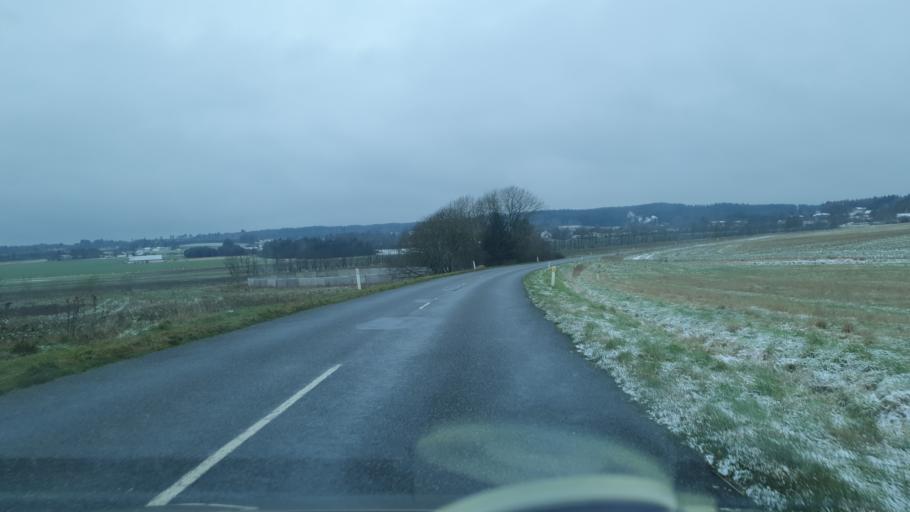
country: DK
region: North Denmark
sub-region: Jammerbugt Kommune
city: Brovst
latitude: 57.1268
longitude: 9.4766
